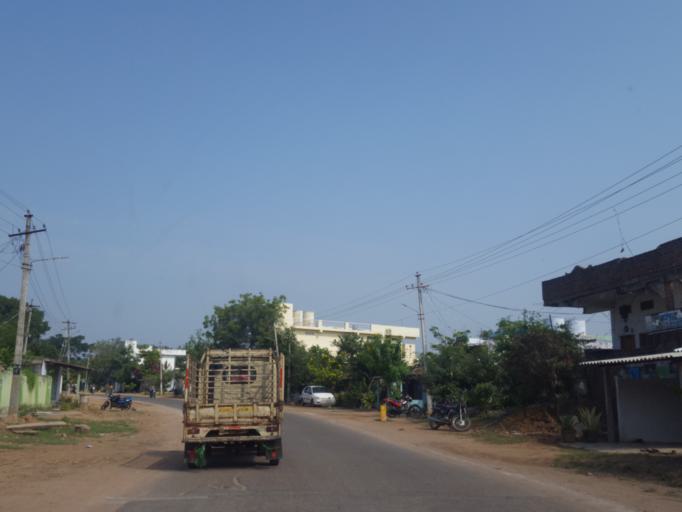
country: IN
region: Telangana
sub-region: Khammam
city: Yellandu
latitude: 17.6011
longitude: 80.3171
